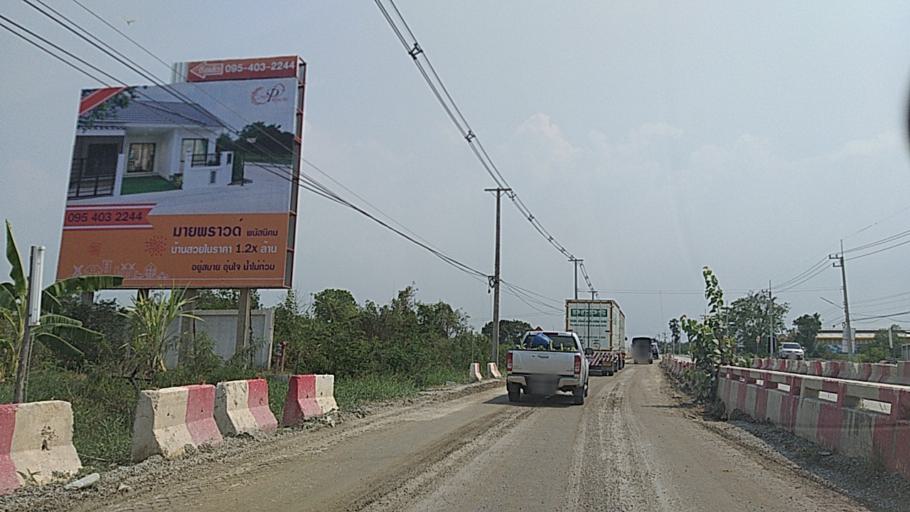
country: TH
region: Chon Buri
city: Phanat Nikhom
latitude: 13.4189
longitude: 101.1872
